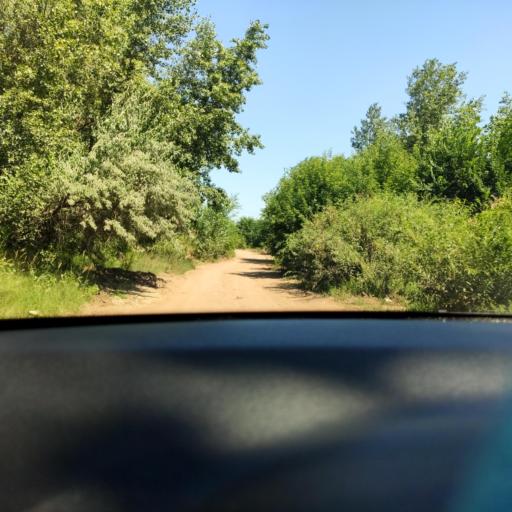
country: RU
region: Samara
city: Smyshlyayevka
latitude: 53.2223
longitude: 50.3440
